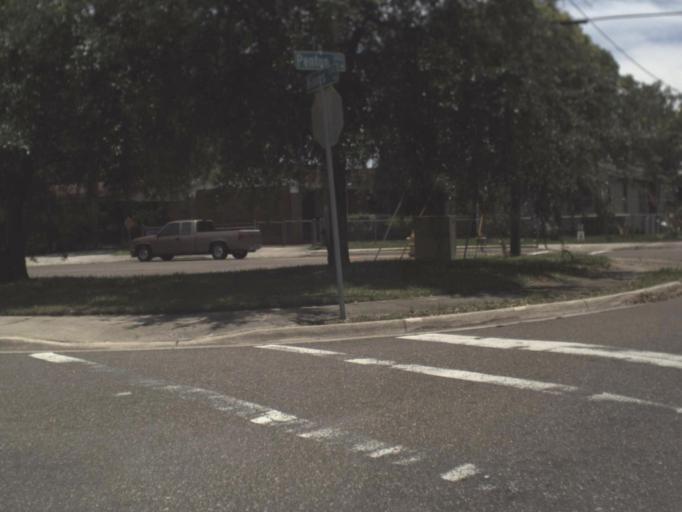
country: US
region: Florida
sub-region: Duval County
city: Jacksonville
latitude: 30.3502
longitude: -81.6999
